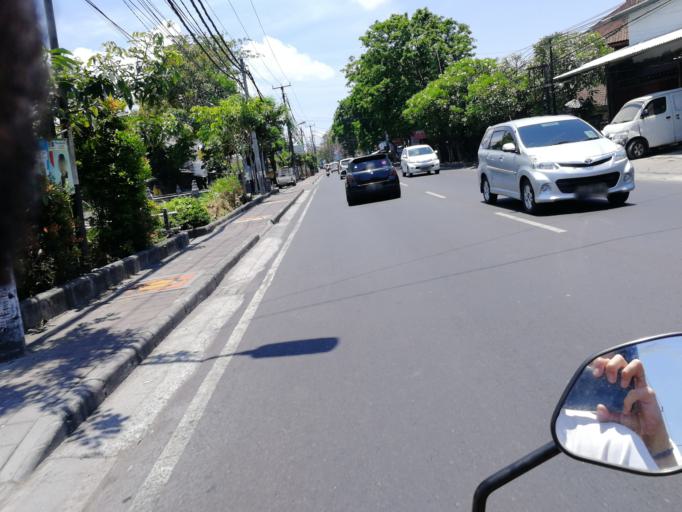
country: ID
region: Bali
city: Karyadharma
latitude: -8.6844
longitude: 115.1950
